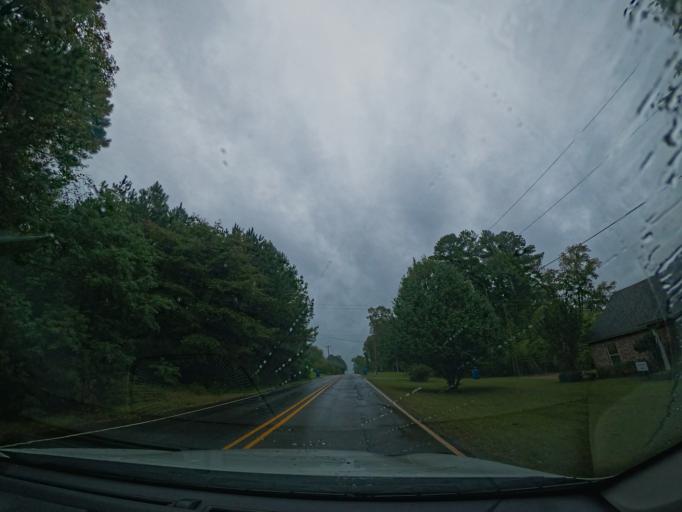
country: US
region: Louisiana
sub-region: Webster Parish
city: Minden
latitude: 32.6393
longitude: -93.2614
